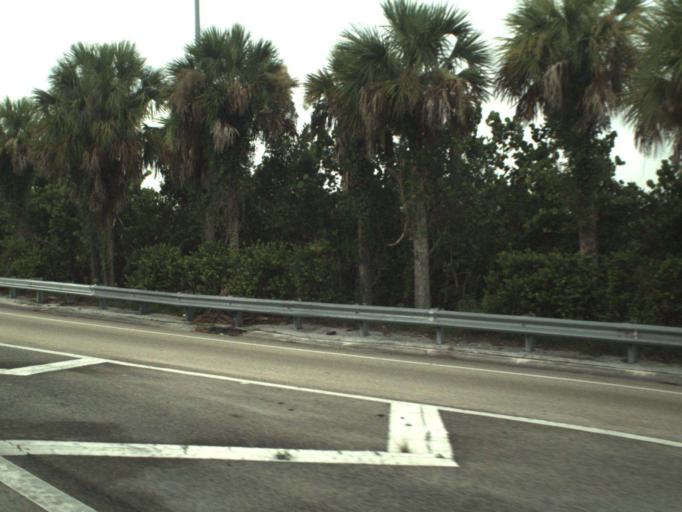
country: US
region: Florida
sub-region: Martin County
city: Palm City
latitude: 27.1096
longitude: -80.2612
